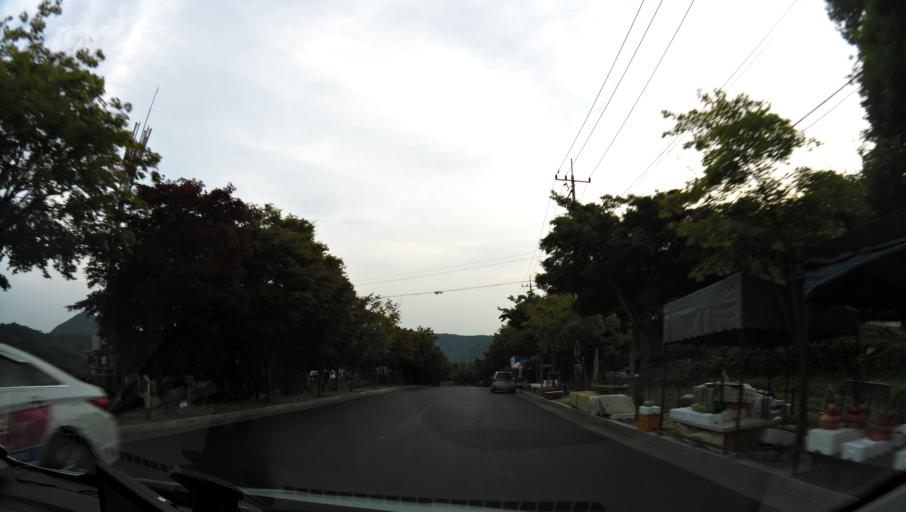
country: KR
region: Daegu
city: Daegu
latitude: 35.9873
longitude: 128.6476
